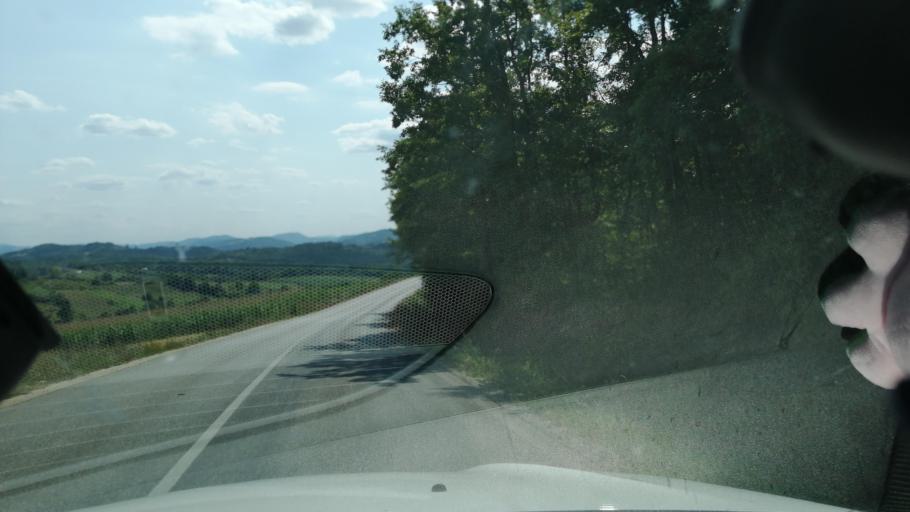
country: RS
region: Central Serbia
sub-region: Moravicki Okrug
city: Cacak
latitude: 43.8123
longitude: 20.2754
